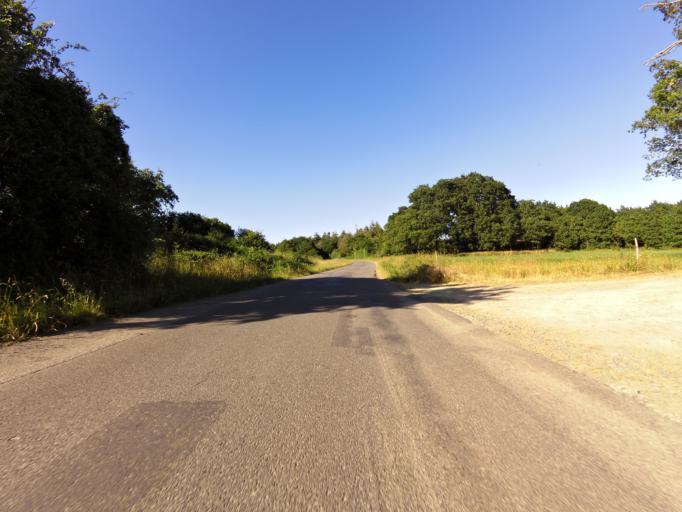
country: FR
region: Brittany
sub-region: Departement du Morbihan
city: Penestin
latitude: 47.4705
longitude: -2.4560
